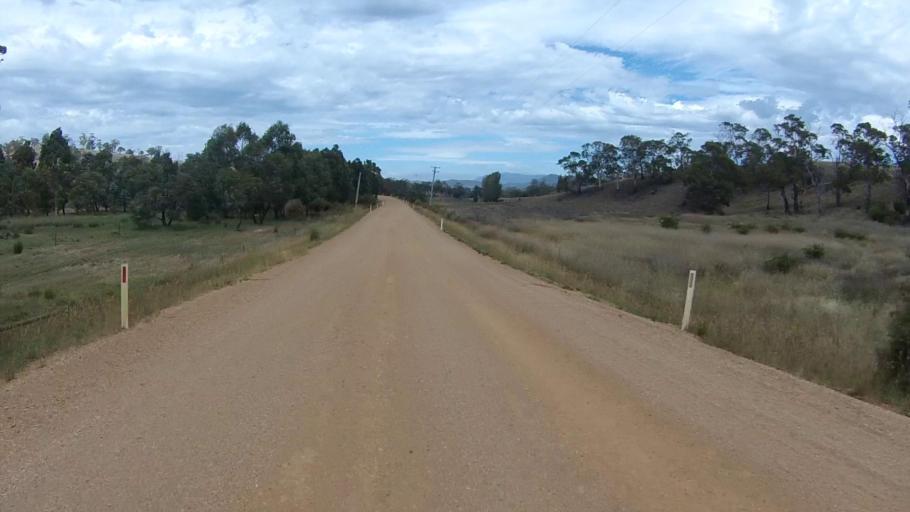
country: AU
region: Tasmania
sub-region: Sorell
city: Sorell
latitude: -42.6935
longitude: 147.4647
